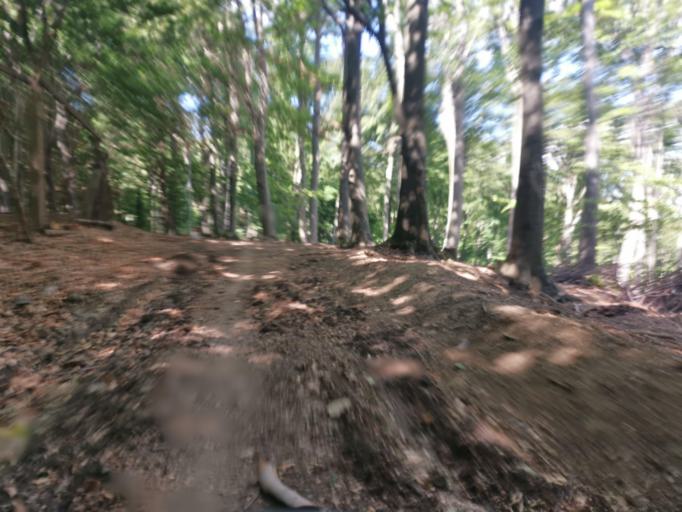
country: CZ
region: South Moravian
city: Knezdub
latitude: 48.8166
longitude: 17.4011
